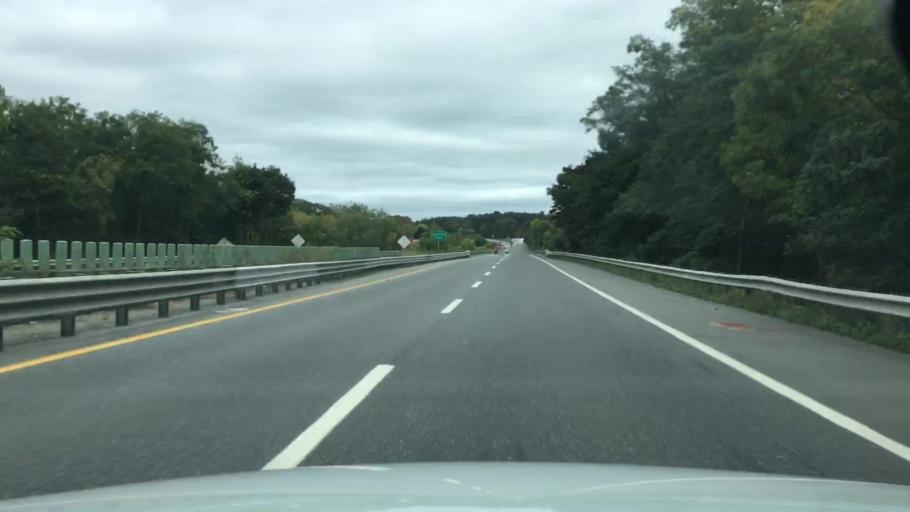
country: US
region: Maine
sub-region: Somerset County
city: Fairfield
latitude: 44.6018
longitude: -69.5958
